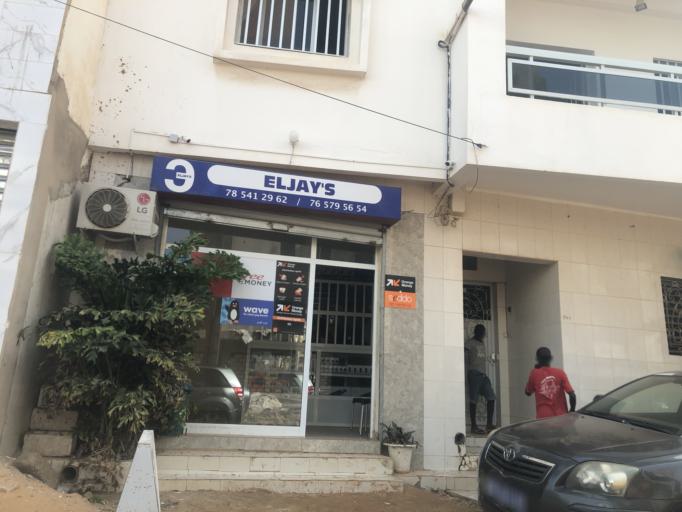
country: SN
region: Dakar
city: Mermoz Boabab
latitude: 14.7329
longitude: -17.4944
